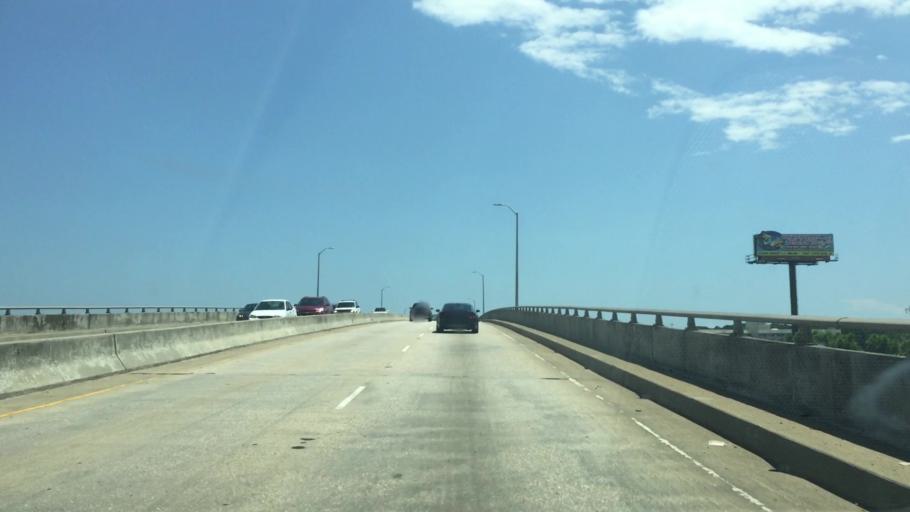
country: US
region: South Carolina
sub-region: Horry County
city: Little River
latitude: 33.8547
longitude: -78.6549
